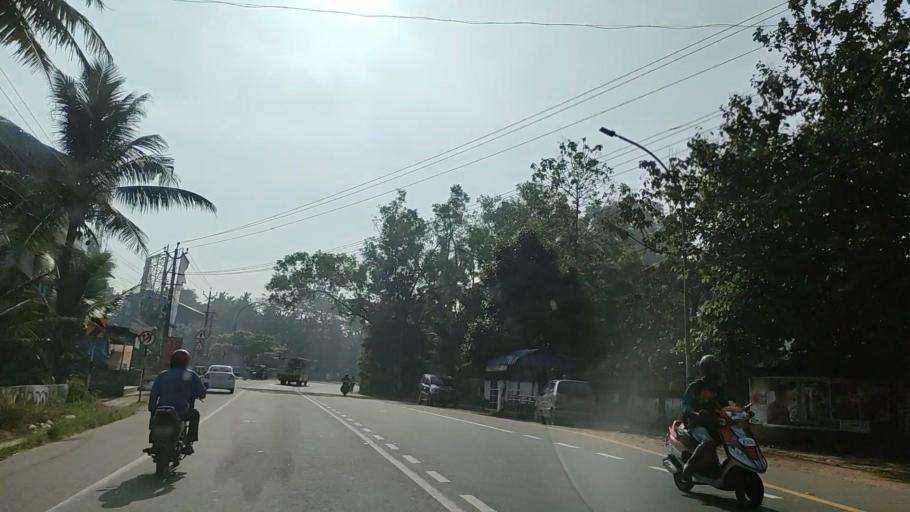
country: IN
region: Kerala
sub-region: Kollam
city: Punalur
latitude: 8.9822
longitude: 76.8091
